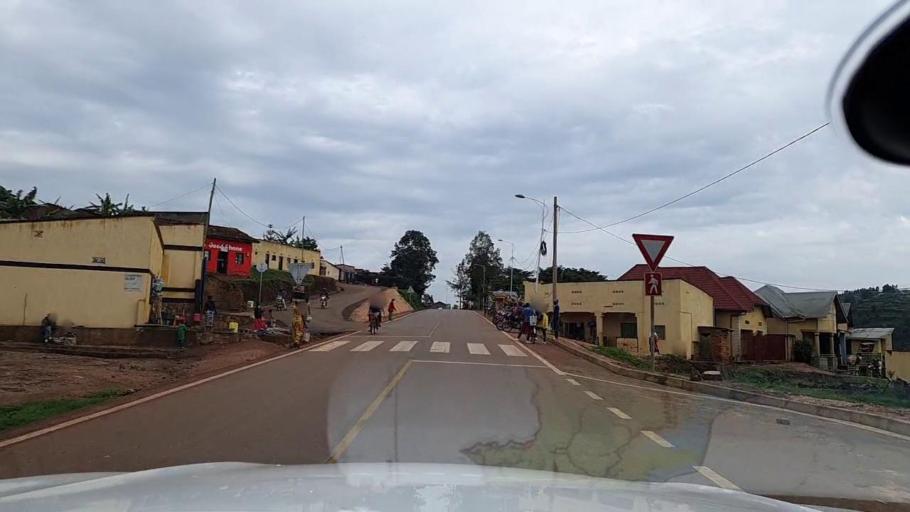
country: RW
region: Southern Province
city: Butare
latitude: -2.5834
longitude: 29.7369
